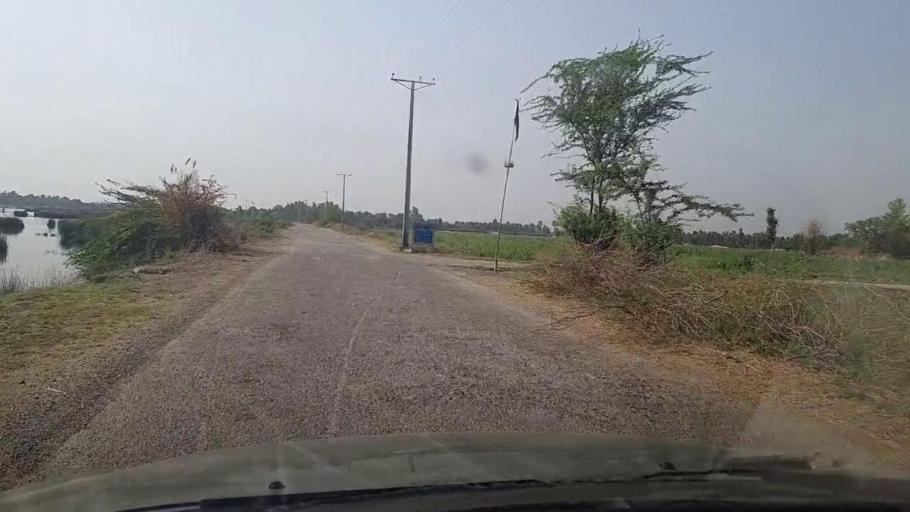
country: PK
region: Sindh
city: Kot Diji
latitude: 27.2870
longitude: 68.6475
